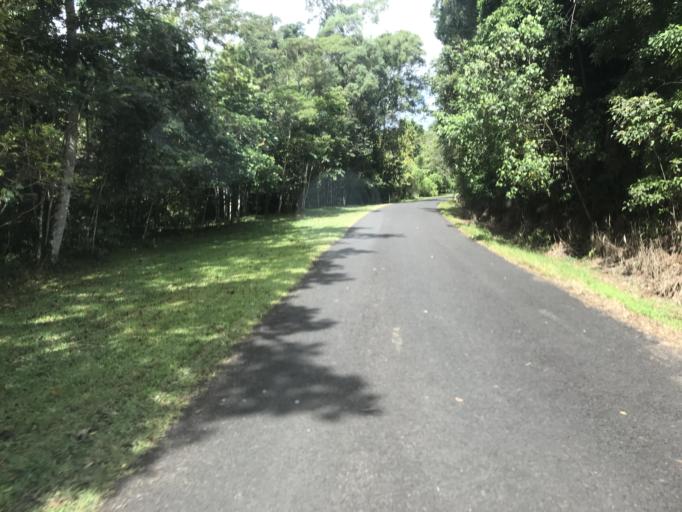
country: AU
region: Queensland
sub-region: Cassowary Coast
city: Innisfail
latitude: -17.5495
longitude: 145.8642
